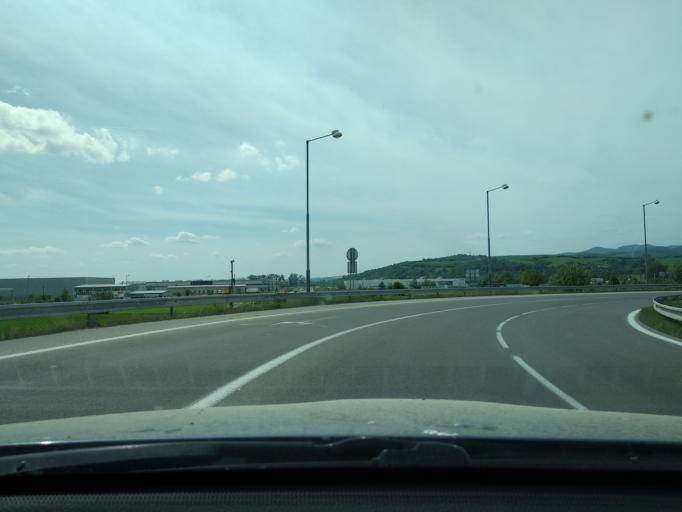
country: SK
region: Trenciansky
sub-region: Okres Trencin
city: Trencin
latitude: 48.8917
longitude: 18.0046
